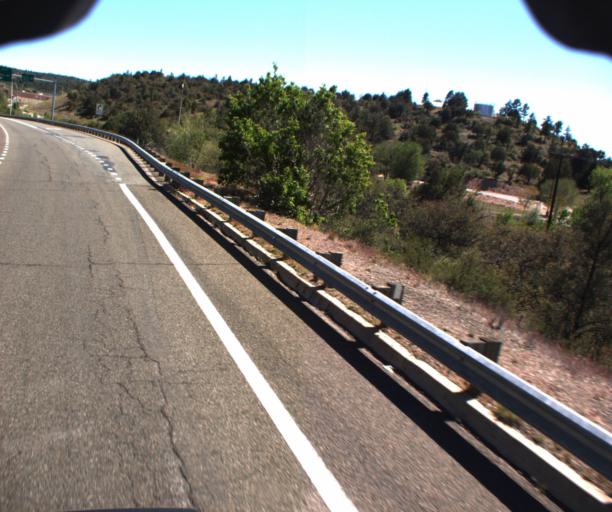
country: US
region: Arizona
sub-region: Yavapai County
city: Prescott
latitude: 34.5527
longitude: -112.4502
